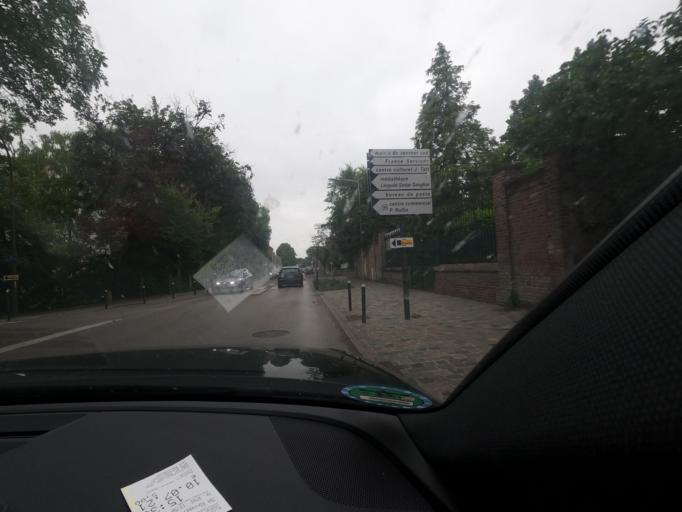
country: FR
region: Picardie
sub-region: Departement de la Somme
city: Amiens
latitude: 49.8744
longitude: 2.3064
